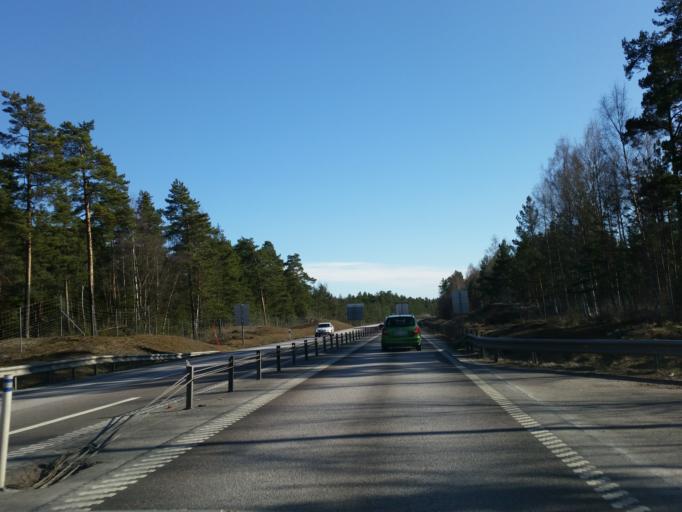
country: SE
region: Kalmar
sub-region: Oskarshamns Kommun
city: Oskarshamn
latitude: 57.2444
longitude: 16.4282
